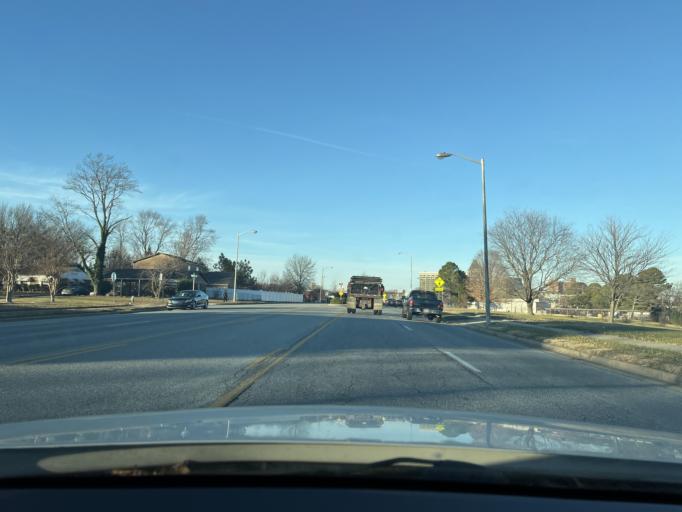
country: US
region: North Carolina
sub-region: Guilford County
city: Greensboro
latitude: 36.0619
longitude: -79.7933
